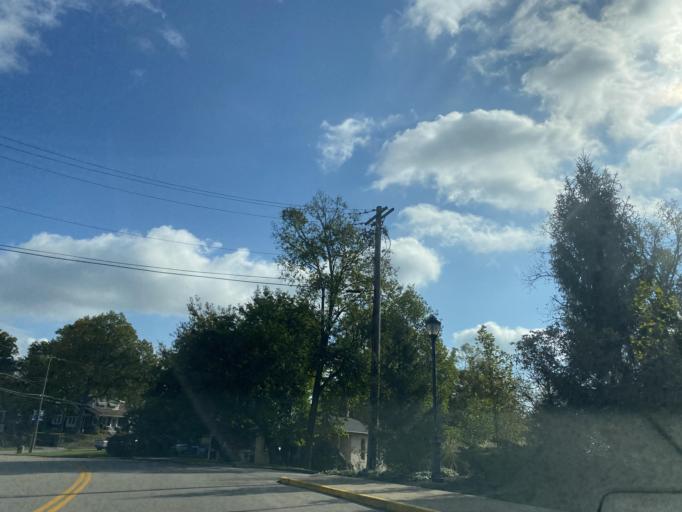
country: US
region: Kentucky
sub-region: Campbell County
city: Fort Thomas
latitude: 39.0855
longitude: -84.4501
